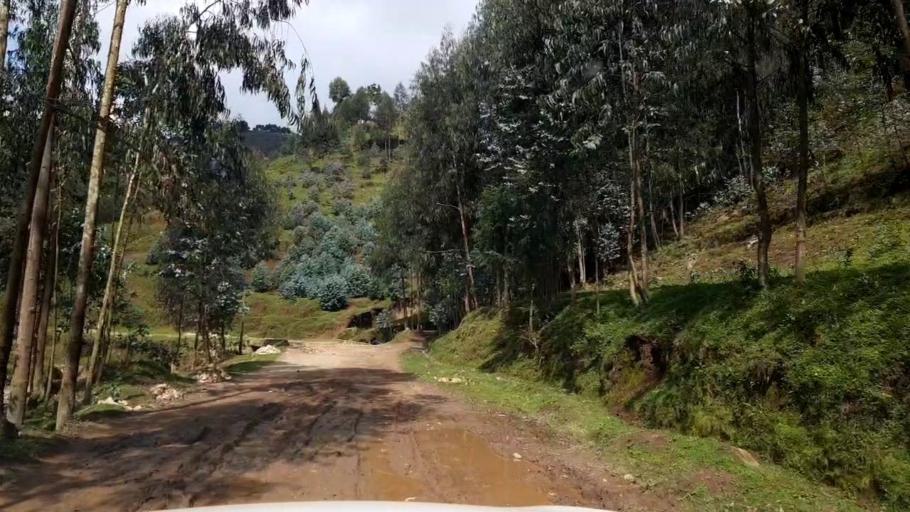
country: RW
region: Western Province
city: Kibuye
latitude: -1.8873
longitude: 29.4682
